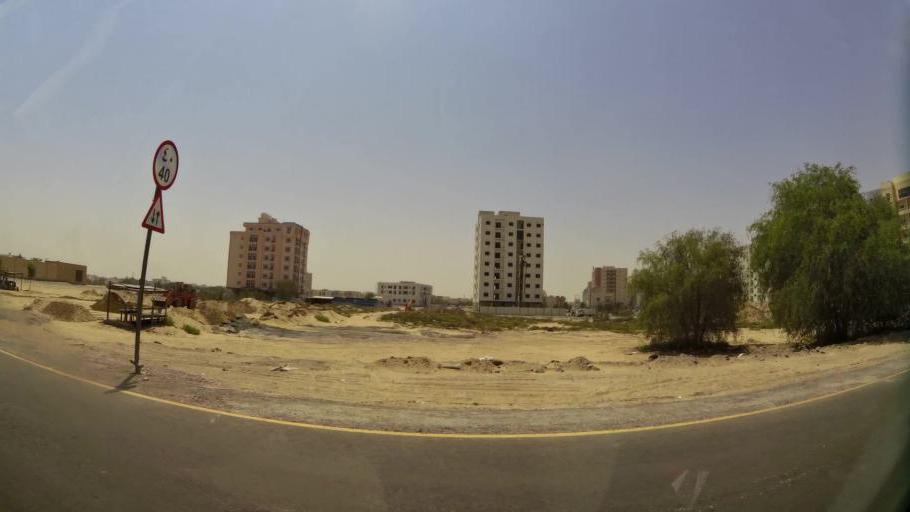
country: AE
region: Ajman
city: Ajman
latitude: 25.4113
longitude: 55.5123
